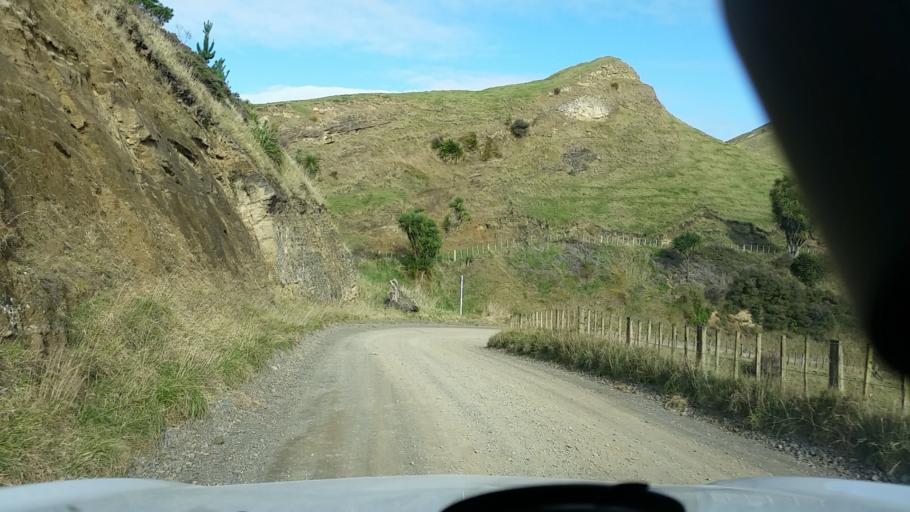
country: NZ
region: Hawke's Bay
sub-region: Napier City
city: Napier
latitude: -39.1109
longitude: 176.8953
